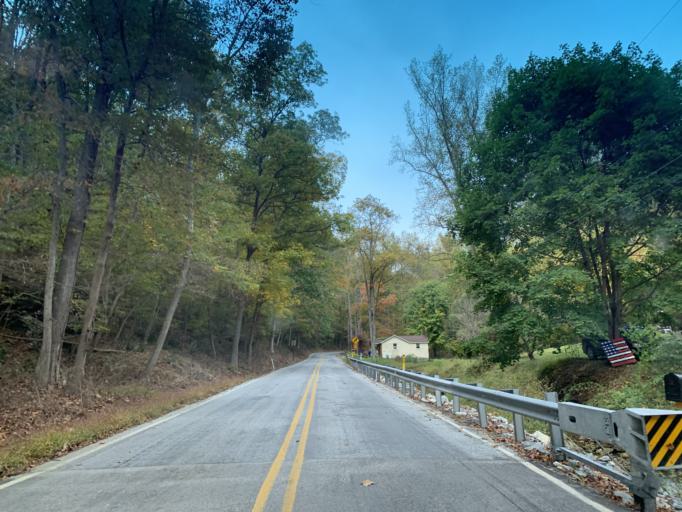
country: US
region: Pennsylvania
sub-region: York County
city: Stewartstown
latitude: 39.8271
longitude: -76.5106
